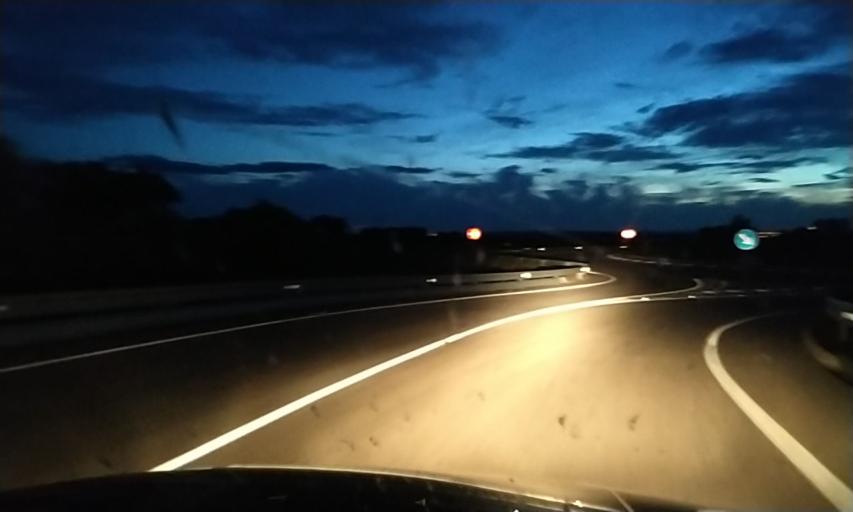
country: ES
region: Extremadura
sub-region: Provincia de Caceres
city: Galisteo
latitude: 39.9753
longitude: -6.2284
